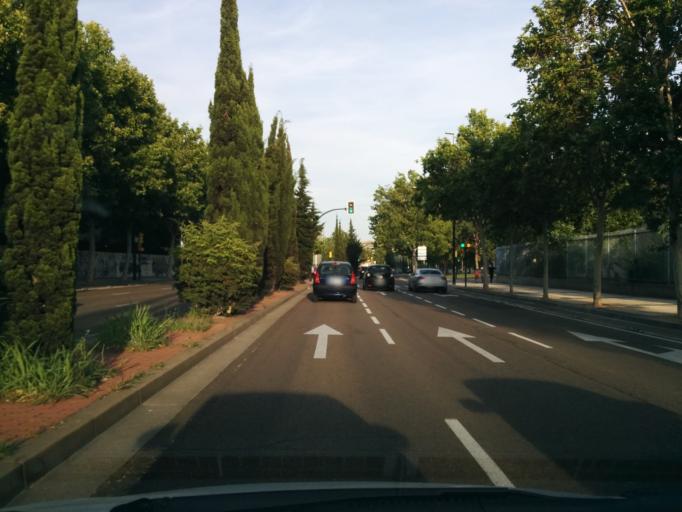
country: ES
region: Aragon
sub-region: Provincia de Zaragoza
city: Zaragoza
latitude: 41.6661
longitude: -0.8698
